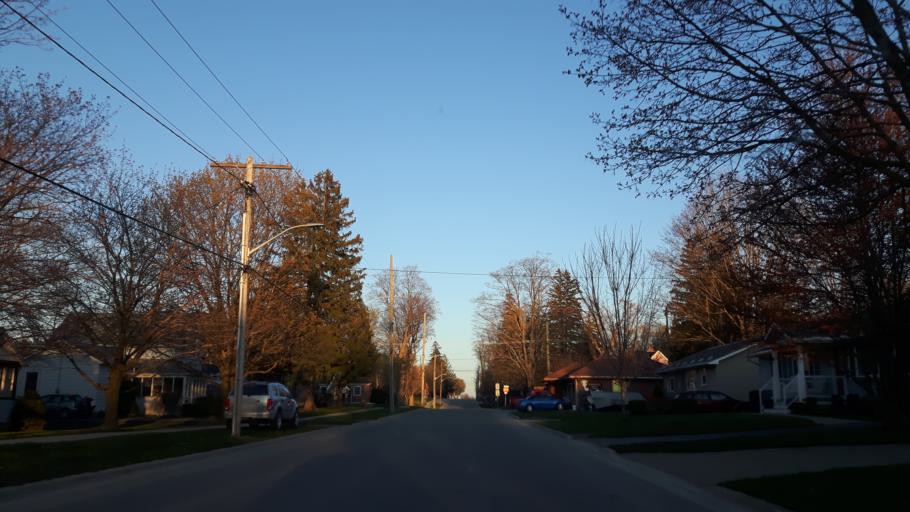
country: CA
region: Ontario
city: Bluewater
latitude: 43.6180
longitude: -81.5370
